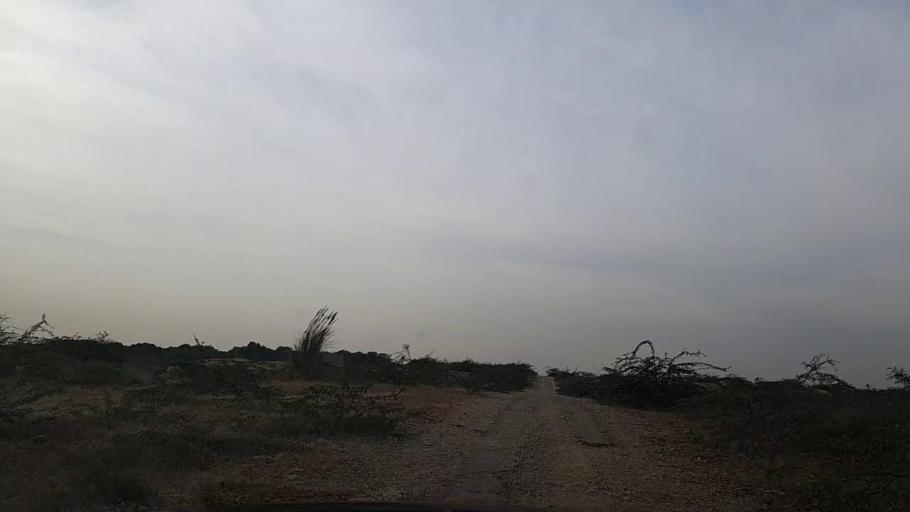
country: PK
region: Sindh
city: Gharo
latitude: 24.7909
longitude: 67.5490
